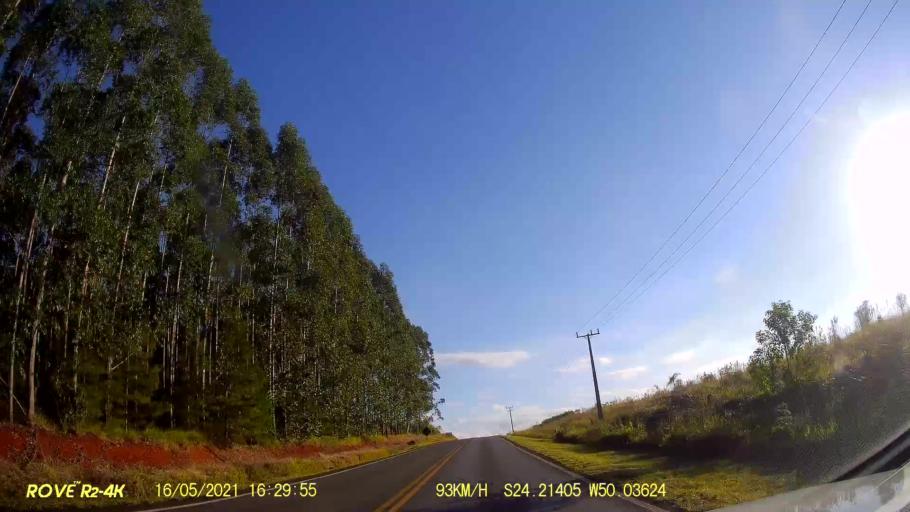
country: BR
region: Parana
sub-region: Pirai Do Sul
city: Pirai do Sul
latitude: -24.2141
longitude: -50.0366
